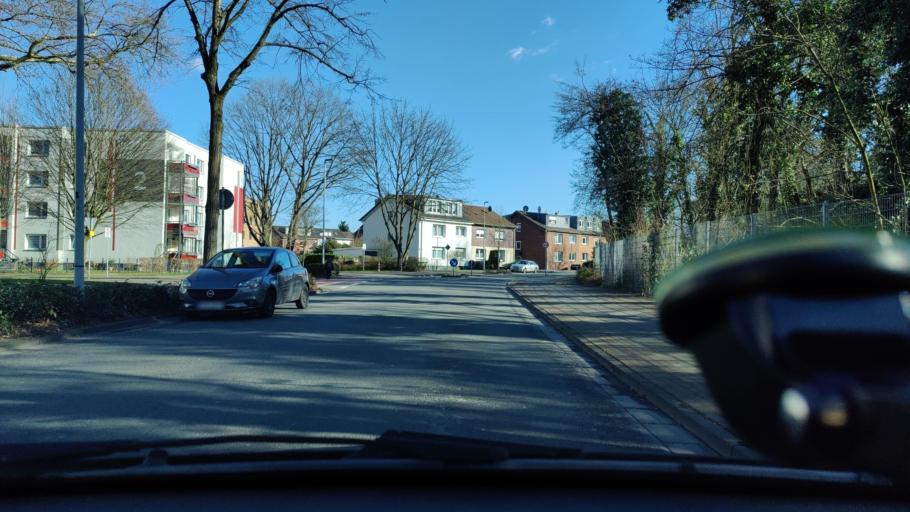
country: DE
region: North Rhine-Westphalia
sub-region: Regierungsbezirk Dusseldorf
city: Dinslaken
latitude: 51.5746
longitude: 6.7416
